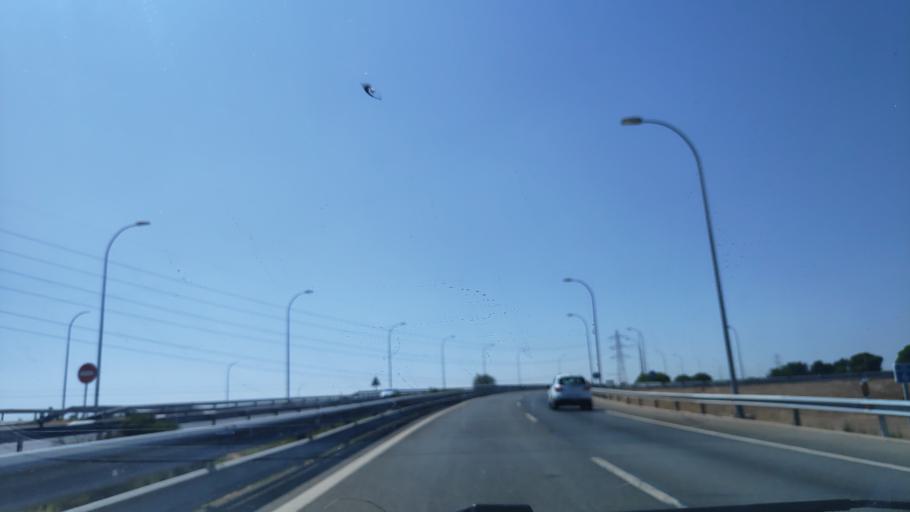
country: ES
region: Madrid
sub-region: Provincia de Madrid
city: Torrejon de la Calzada
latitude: 40.1985
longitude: -3.7893
